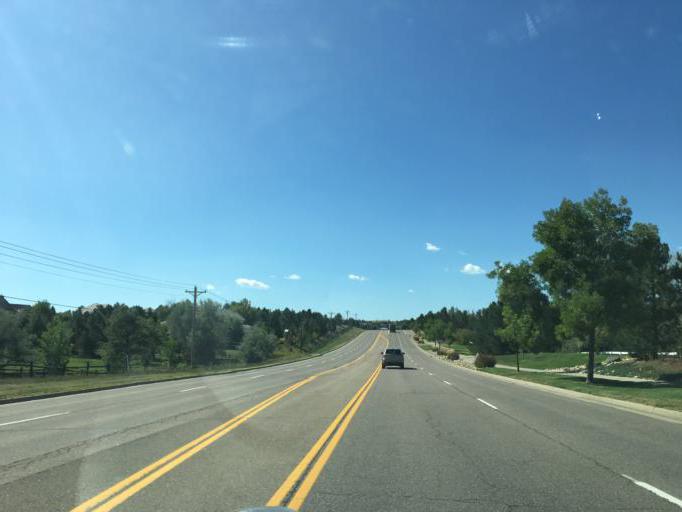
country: US
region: Colorado
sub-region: Douglas County
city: Parker
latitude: 39.6036
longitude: -104.7449
